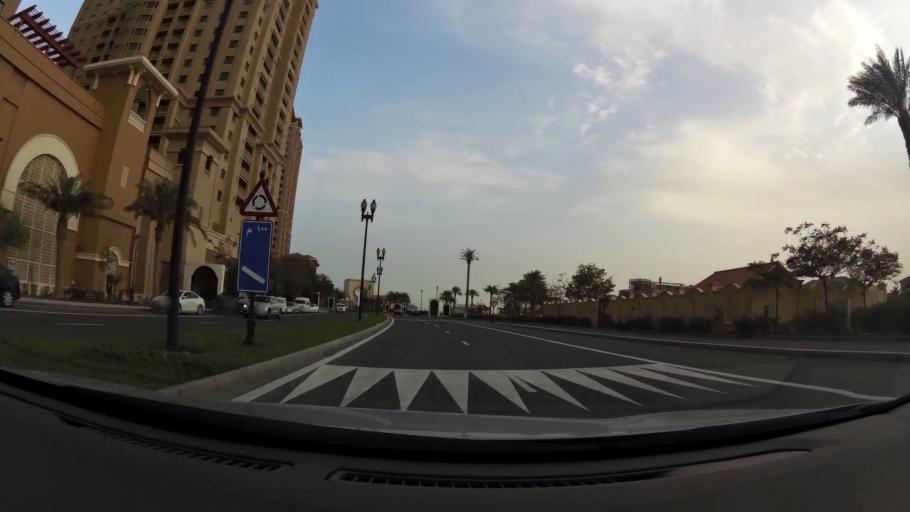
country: QA
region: Baladiyat ad Dawhah
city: Doha
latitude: 25.3672
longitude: 51.5385
